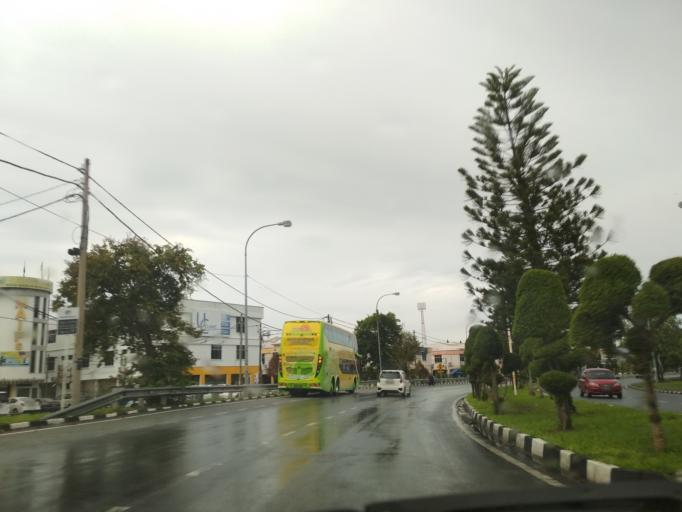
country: MY
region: Perlis
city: Kangar
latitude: 6.4359
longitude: 100.1885
